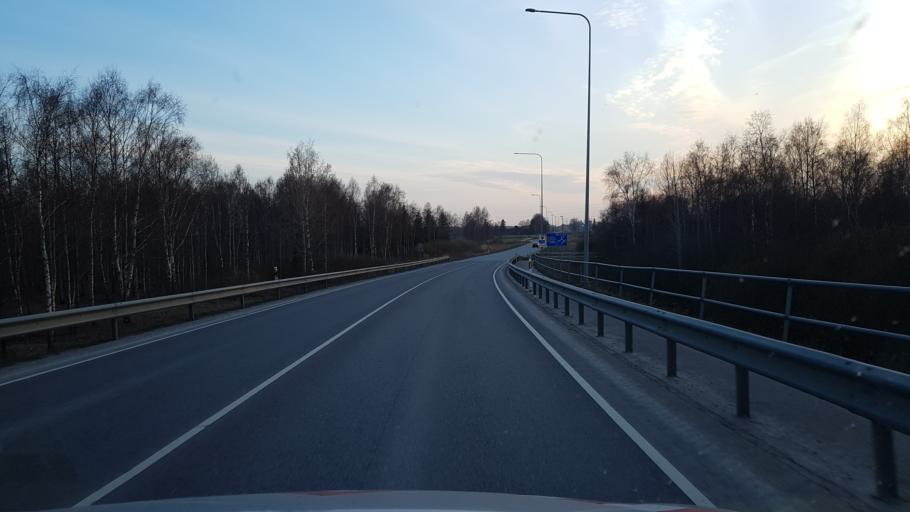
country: EE
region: Laeaene-Virumaa
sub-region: Someru vald
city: Someru
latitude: 59.3574
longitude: 26.4032
